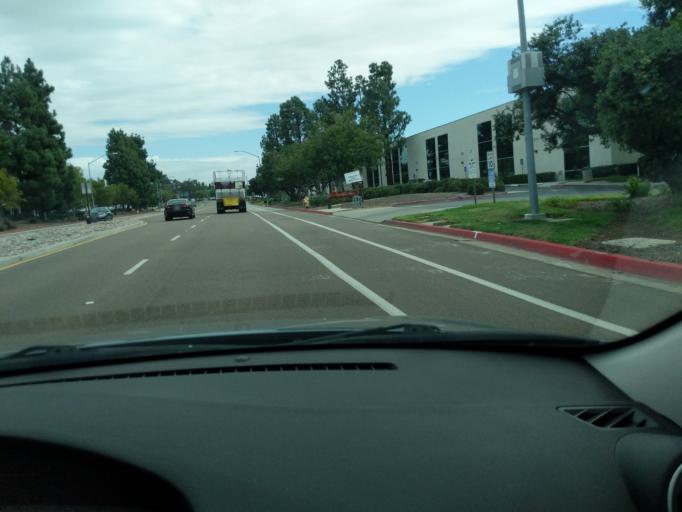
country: US
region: California
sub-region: San Diego County
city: San Diego
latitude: 32.8212
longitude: -117.1432
